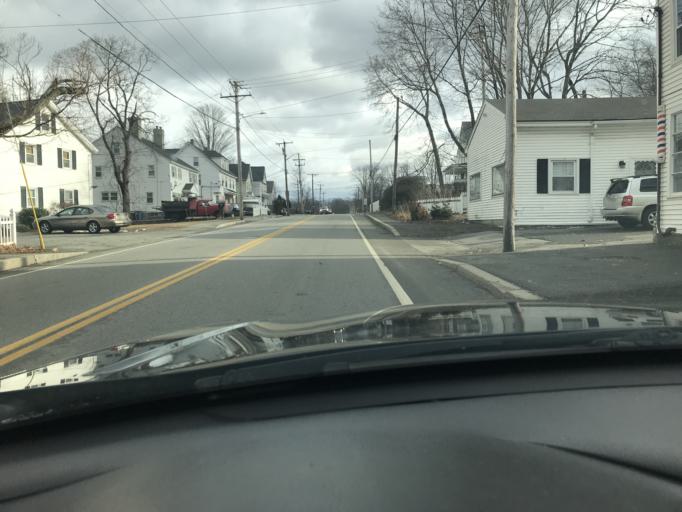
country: US
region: Massachusetts
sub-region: Middlesex County
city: Chelmsford
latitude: 42.6372
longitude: -71.3766
